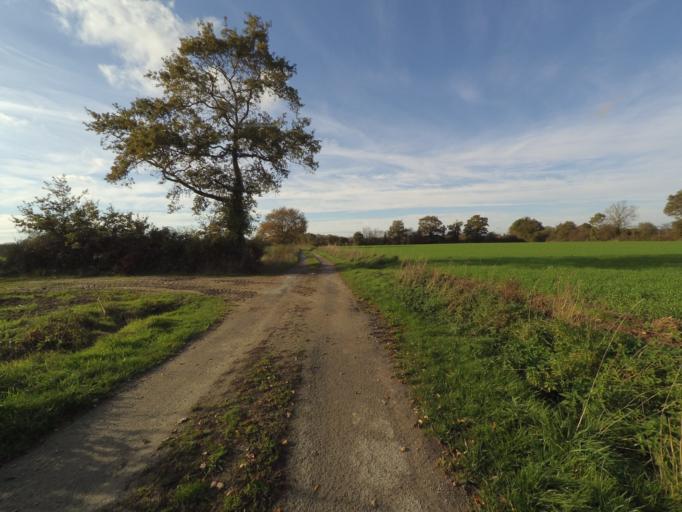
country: FR
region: Pays de la Loire
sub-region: Departement de la Vendee
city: Saint-Hilaire-de-Loulay
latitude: 47.0091
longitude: -1.3517
